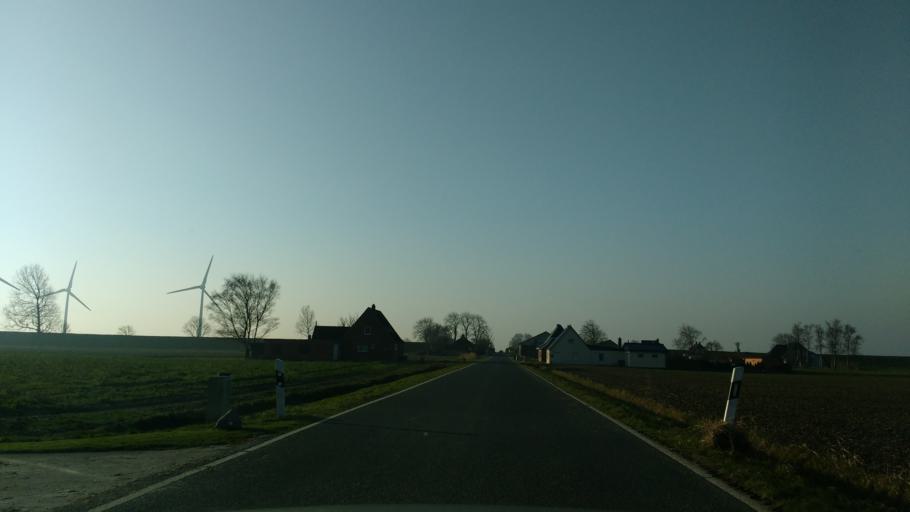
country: DE
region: Schleswig-Holstein
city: Friedrichskoog
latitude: 53.9882
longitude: 8.9299
